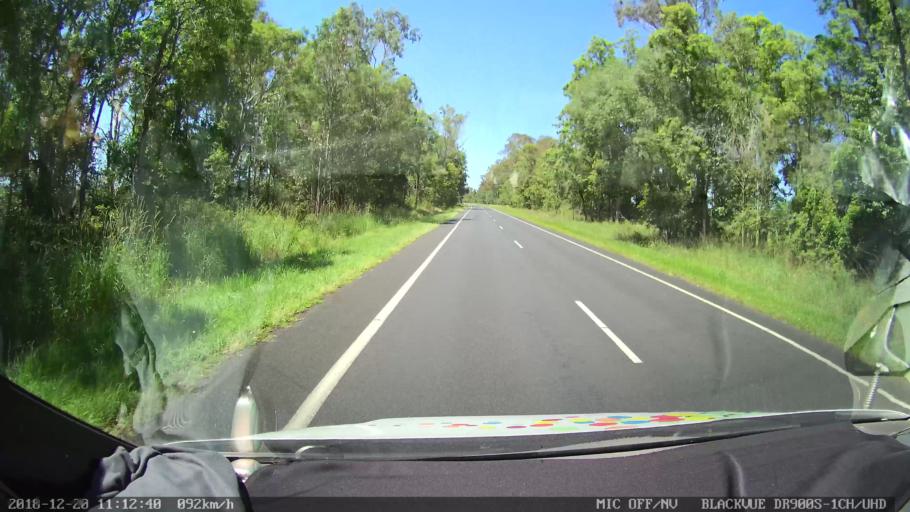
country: AU
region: New South Wales
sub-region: Richmond Valley
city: Casino
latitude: -28.9772
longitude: 153.0103
